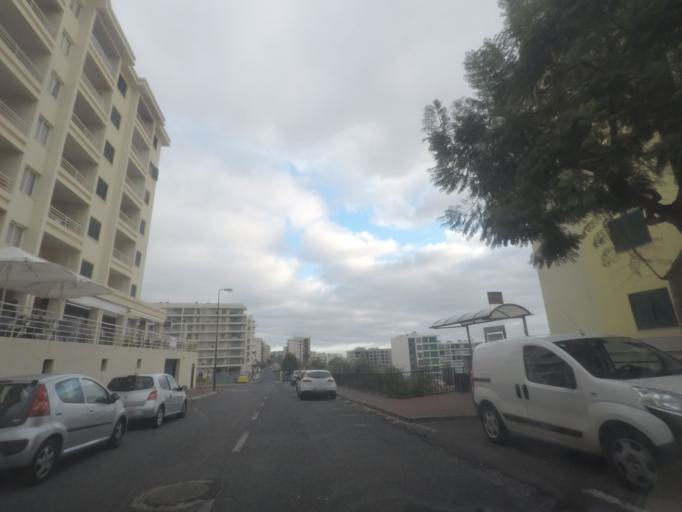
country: PT
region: Madeira
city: Camara de Lobos
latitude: 32.6424
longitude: -16.9485
